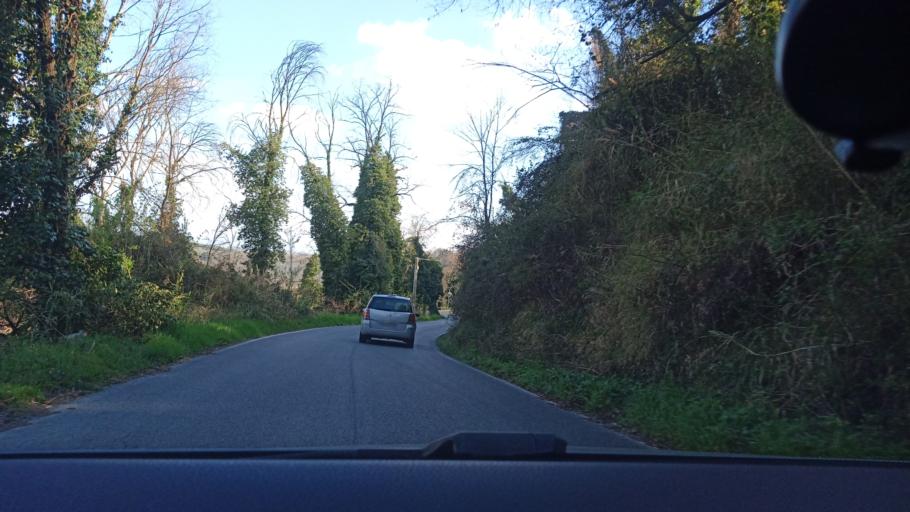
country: IT
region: Latium
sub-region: Citta metropolitana di Roma Capitale
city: Torrita Tiberina
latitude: 42.2413
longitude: 12.6218
